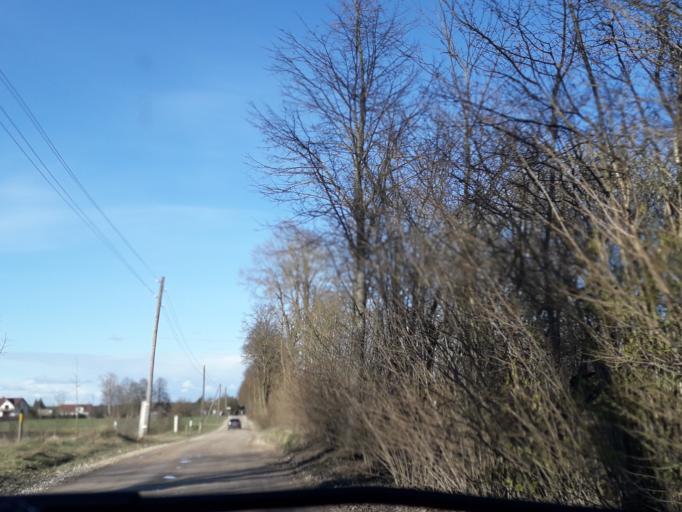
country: LV
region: Kekava
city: Kekava
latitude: 56.8433
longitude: 24.2014
